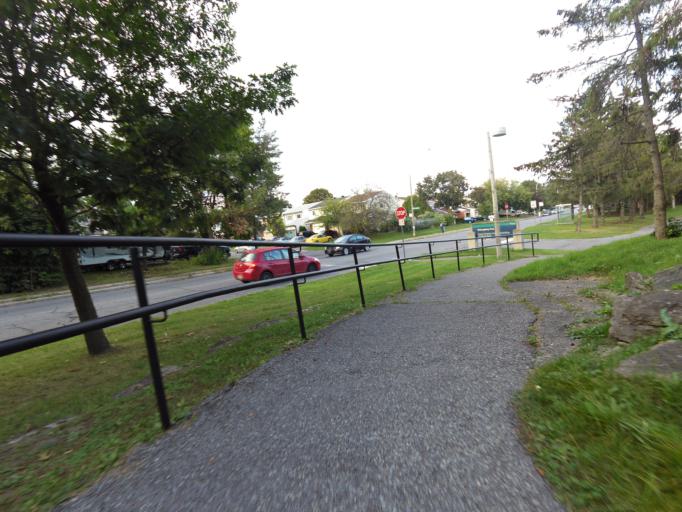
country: CA
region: Ontario
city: Bells Corners
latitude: 45.2736
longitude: -75.7525
